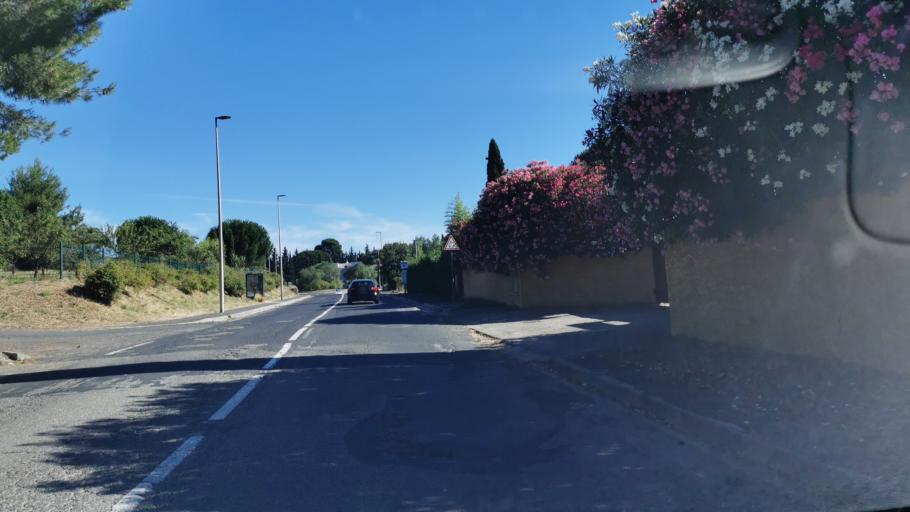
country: FR
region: Languedoc-Roussillon
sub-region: Departement de l'Herault
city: Beziers
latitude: 43.3597
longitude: 3.2125
